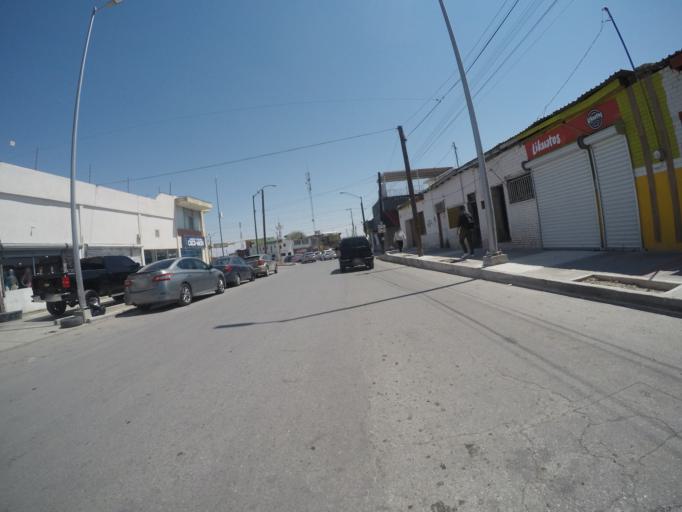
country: MX
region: Chihuahua
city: Ciudad Juarez
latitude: 31.7333
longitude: -106.4857
